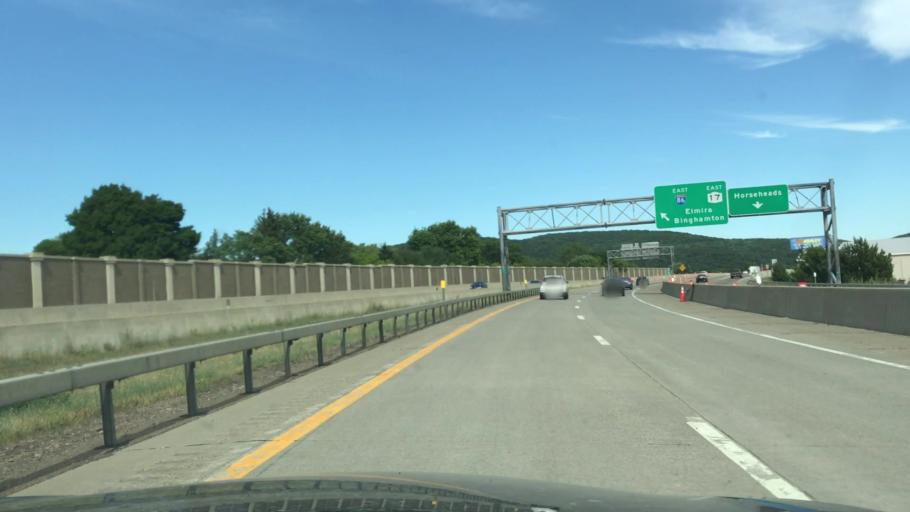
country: US
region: New York
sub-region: Chemung County
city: Horseheads
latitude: 42.1599
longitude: -76.8320
